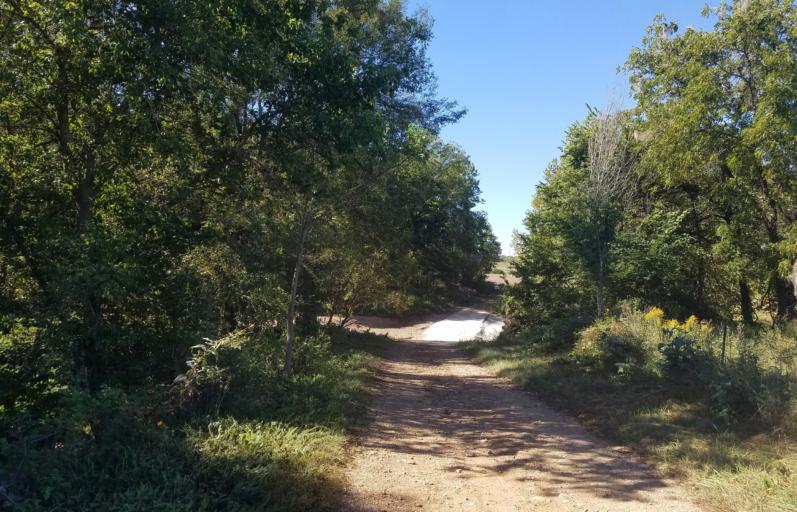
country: US
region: Missouri
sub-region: Cooper County
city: Boonville
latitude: 38.8554
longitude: -92.6583
